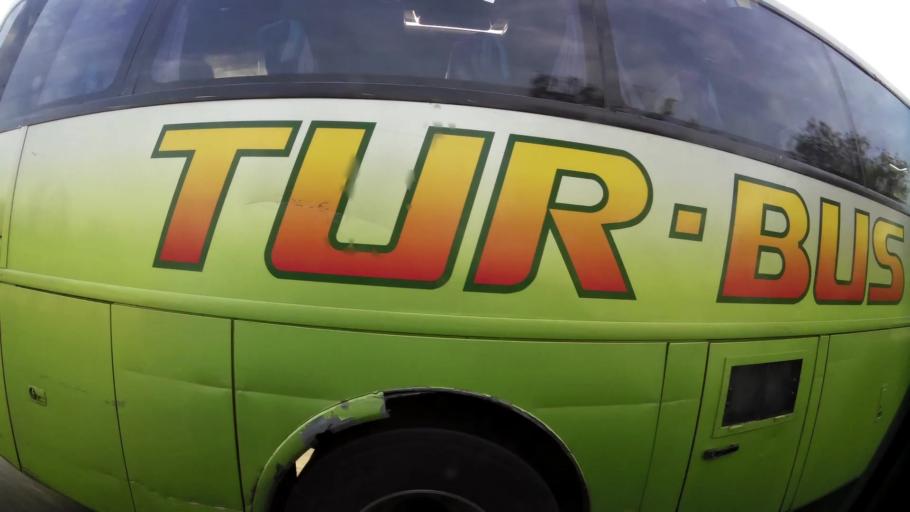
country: CL
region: Santiago Metropolitan
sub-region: Provincia de Santiago
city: Santiago
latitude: -33.4952
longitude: -70.6920
